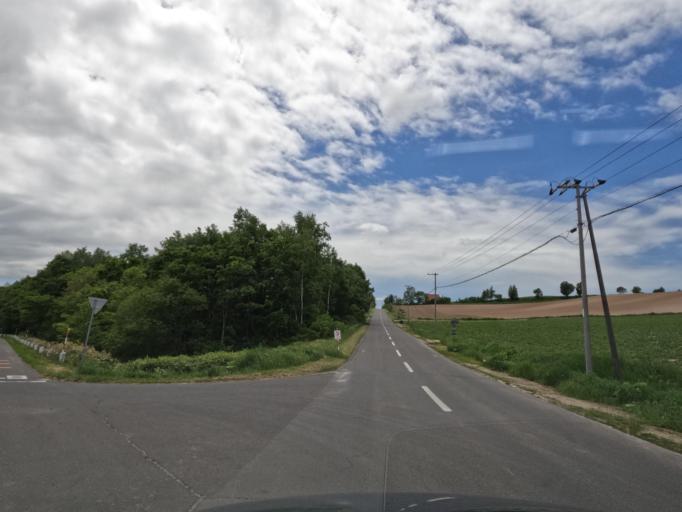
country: JP
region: Hokkaido
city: Shimo-furano
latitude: 43.5249
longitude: 142.4344
